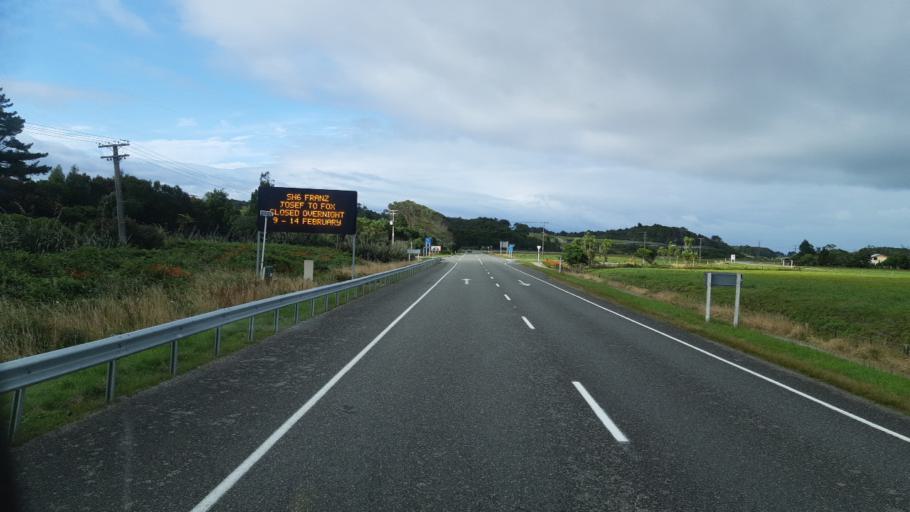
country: NZ
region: West Coast
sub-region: Westland District
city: Hokitika
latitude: -42.7285
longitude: 170.9597
